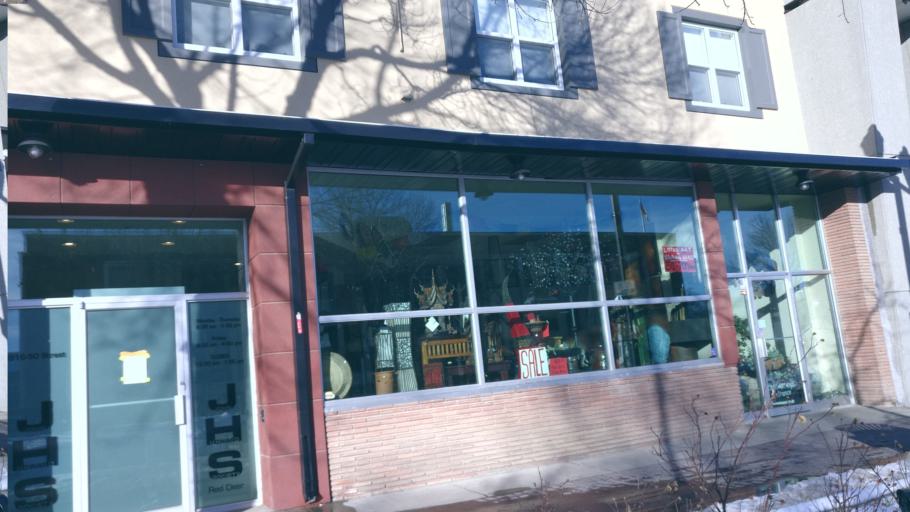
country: CA
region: Alberta
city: Red Deer
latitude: 52.2691
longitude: -113.8125
